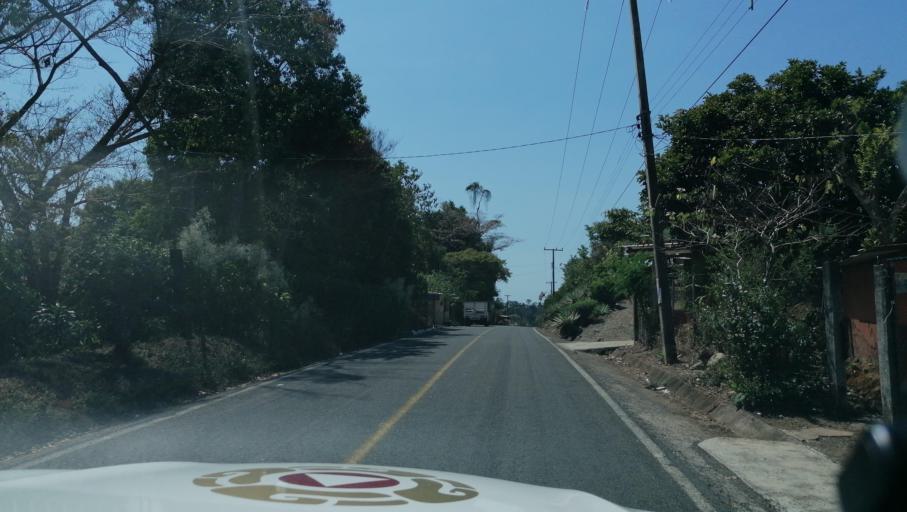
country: MX
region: Chiapas
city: Veinte de Noviembre
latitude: 14.9971
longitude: -92.2332
